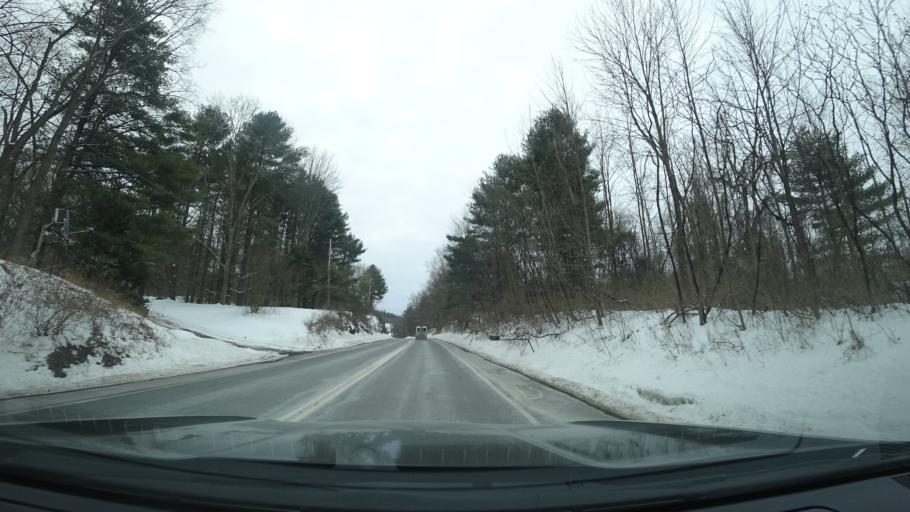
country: US
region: New York
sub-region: Washington County
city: Fort Edward
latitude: 43.2109
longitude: -73.4877
